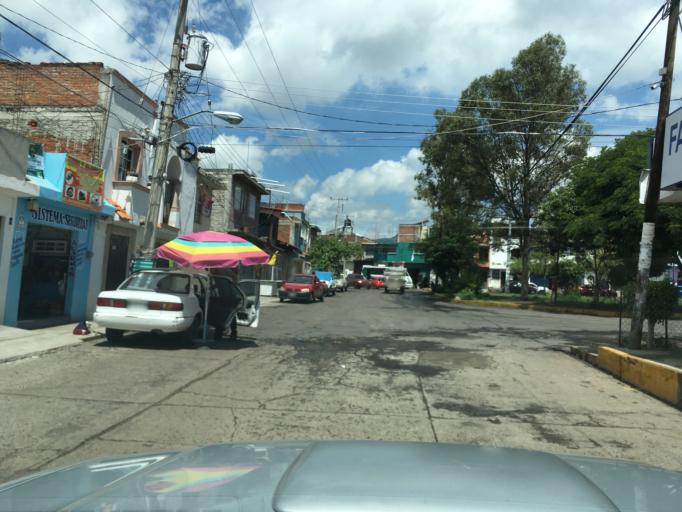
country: MX
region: Michoacan
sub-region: Tarimbaro
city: Real Hacienda (Metropolis)
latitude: 19.7299
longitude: -101.2062
